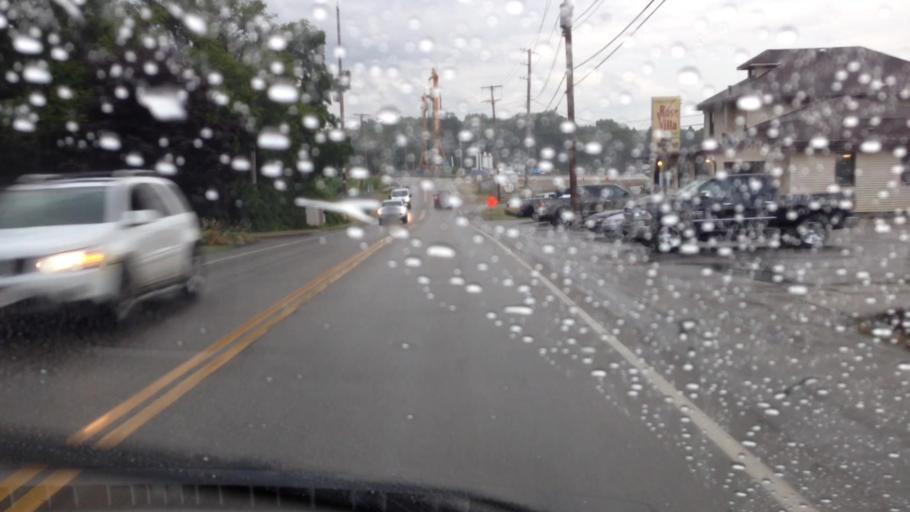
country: US
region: Ohio
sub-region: Summit County
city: Portage Lakes
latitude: 40.9966
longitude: -81.5341
